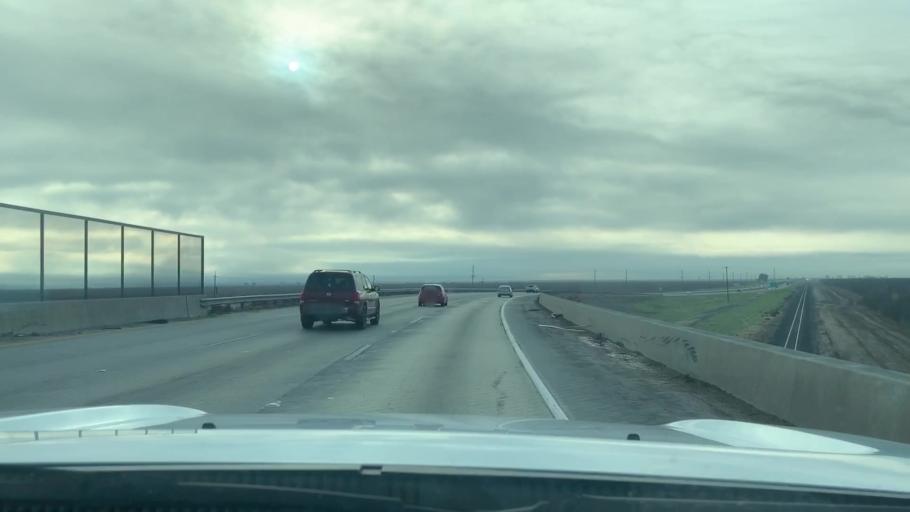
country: US
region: California
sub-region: Kern County
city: McFarland
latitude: 35.5907
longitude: -119.2062
